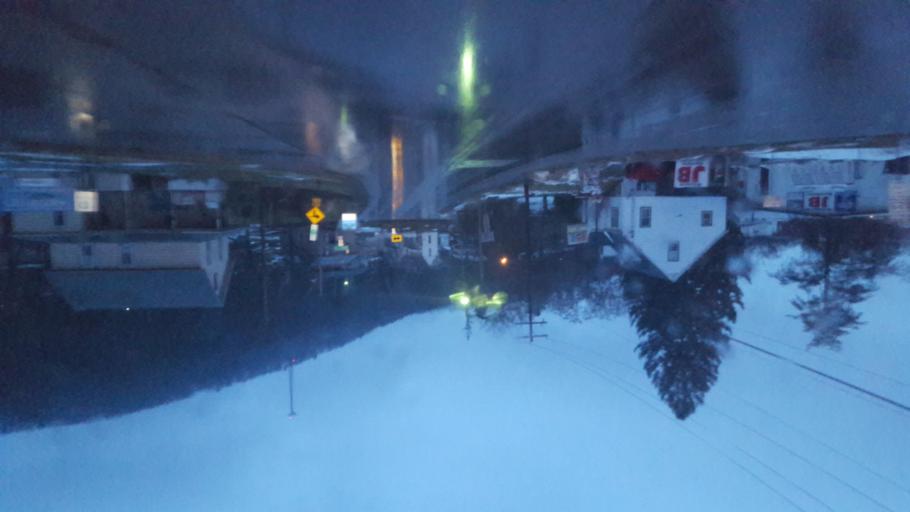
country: US
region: Pennsylvania
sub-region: McKean County
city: Smethport
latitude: 41.8114
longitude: -78.4336
